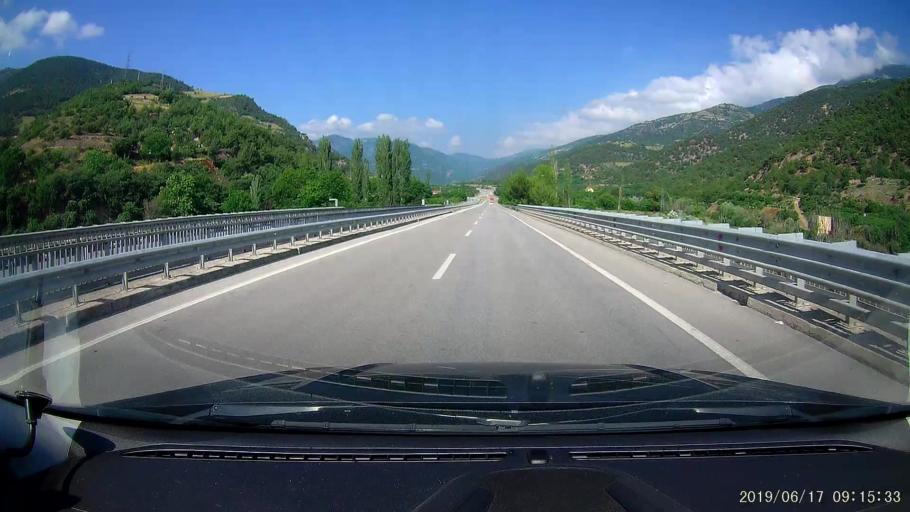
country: TR
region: Amasya
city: Akdag
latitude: 40.7466
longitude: 36.0338
